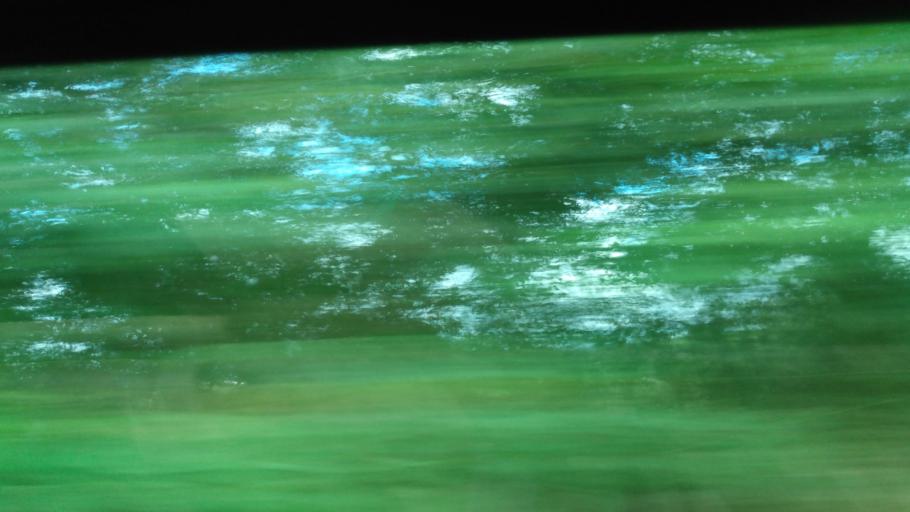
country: BR
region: Pernambuco
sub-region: Quipapa
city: Quipapa
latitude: -8.7839
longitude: -35.9539
